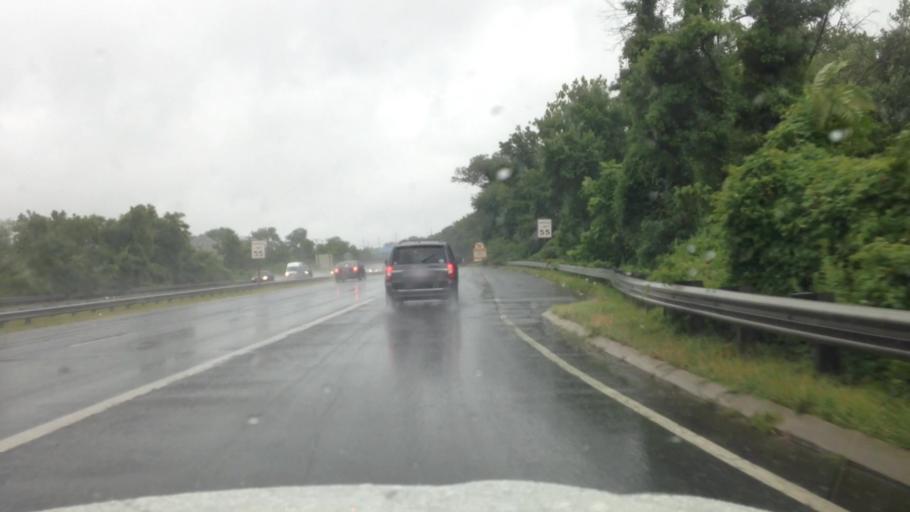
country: US
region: Maryland
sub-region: Prince George's County
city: Cheverly
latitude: 38.9179
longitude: -76.9294
